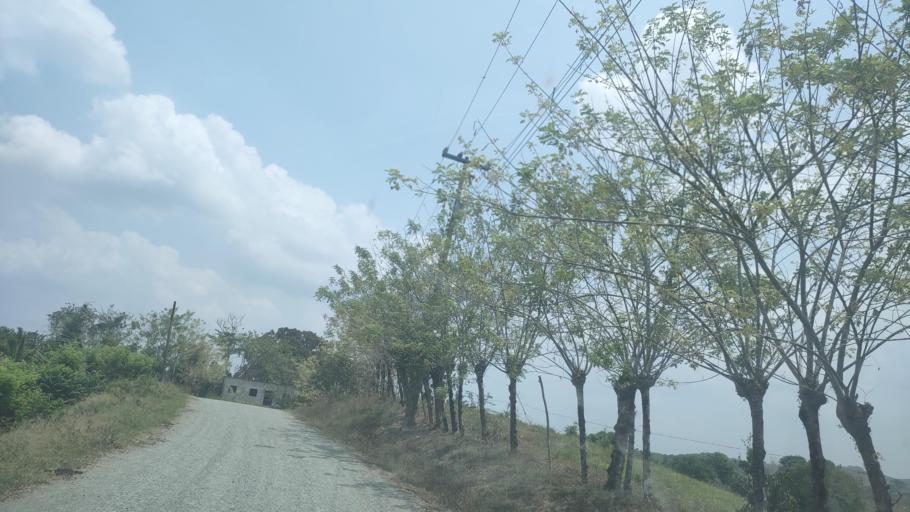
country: MX
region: Tabasco
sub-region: Huimanguillo
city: Francisco Rueda
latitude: 17.5893
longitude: -93.9584
